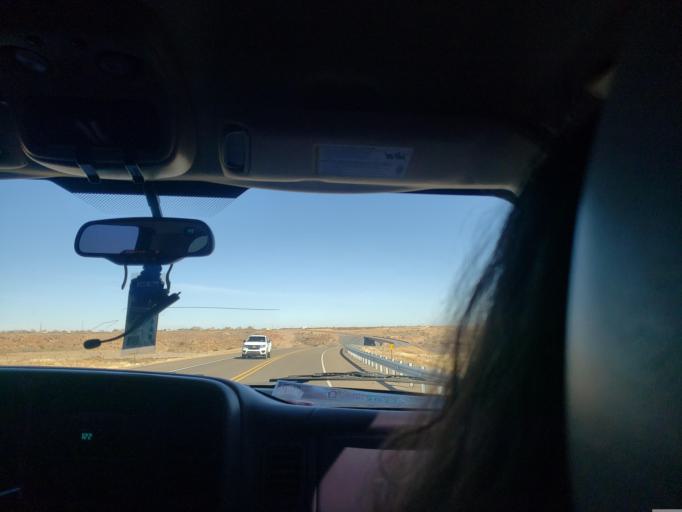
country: US
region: New Mexico
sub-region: Quay County
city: Logan
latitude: 35.3511
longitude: -103.4190
